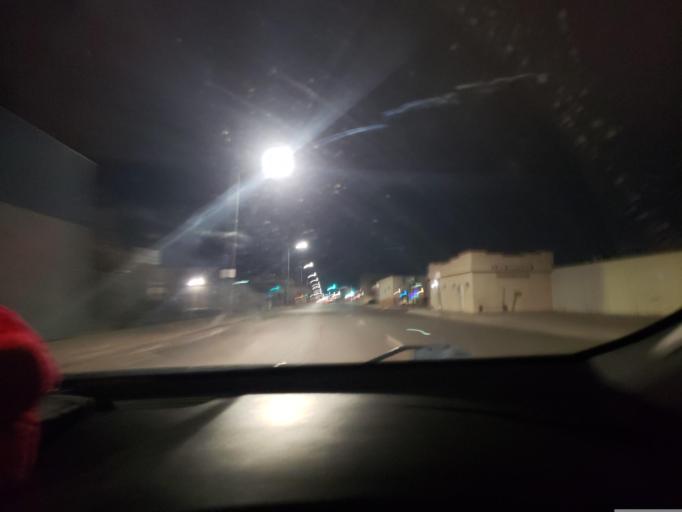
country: US
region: New Mexico
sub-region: Bernalillo County
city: Albuquerque
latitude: 35.0931
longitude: -106.6477
